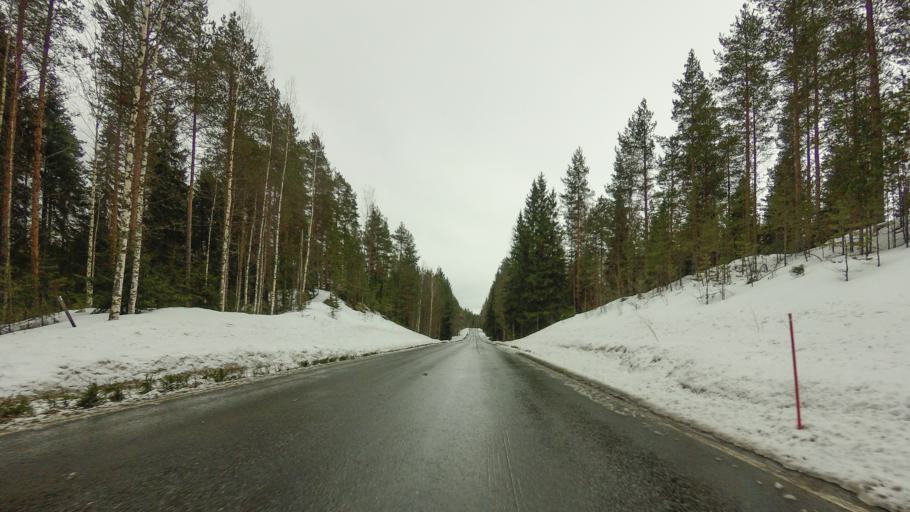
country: FI
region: Southern Savonia
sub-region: Savonlinna
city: Savonlinna
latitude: 61.9818
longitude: 28.8095
